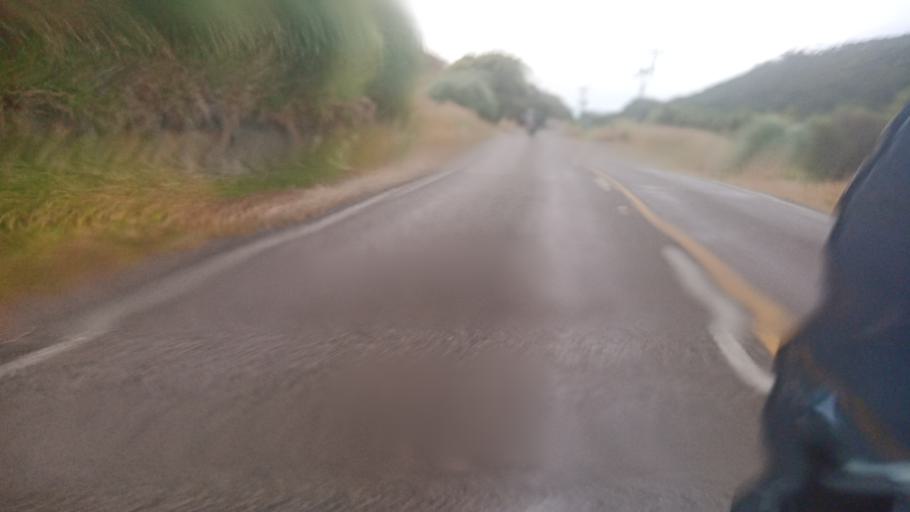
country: NZ
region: Bay of Plenty
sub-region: Opotiki District
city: Opotiki
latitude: -37.9461
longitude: 177.5013
